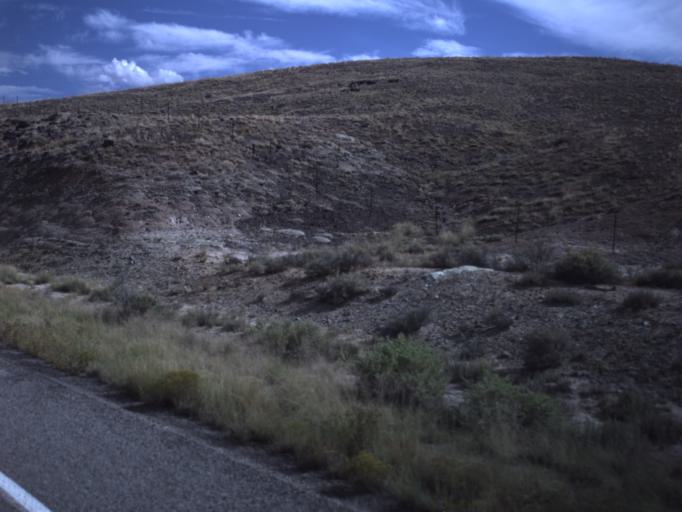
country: US
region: Colorado
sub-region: Montezuma County
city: Towaoc
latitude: 37.1738
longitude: -109.1003
